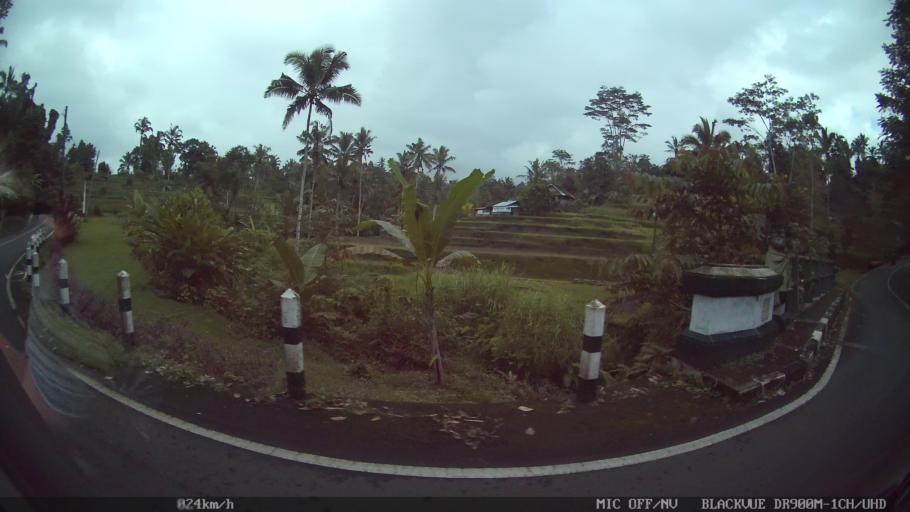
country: ID
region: Bali
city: Peneng
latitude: -8.3621
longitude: 115.1826
